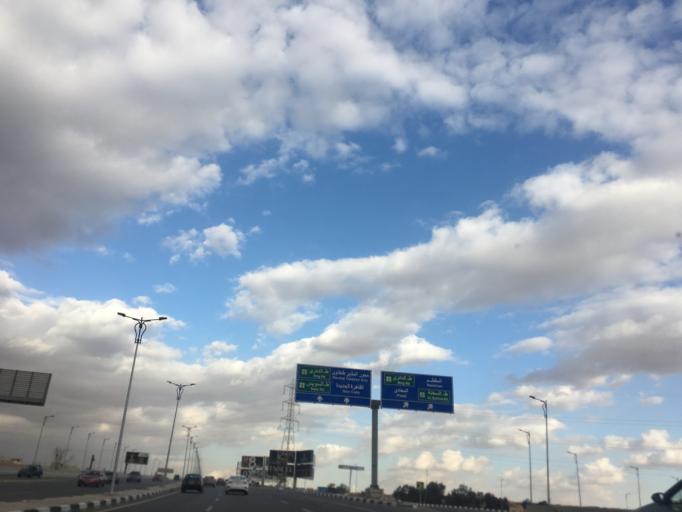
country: EG
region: Muhafazat al Qahirah
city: Cairo
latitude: 30.0186
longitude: 31.3413
